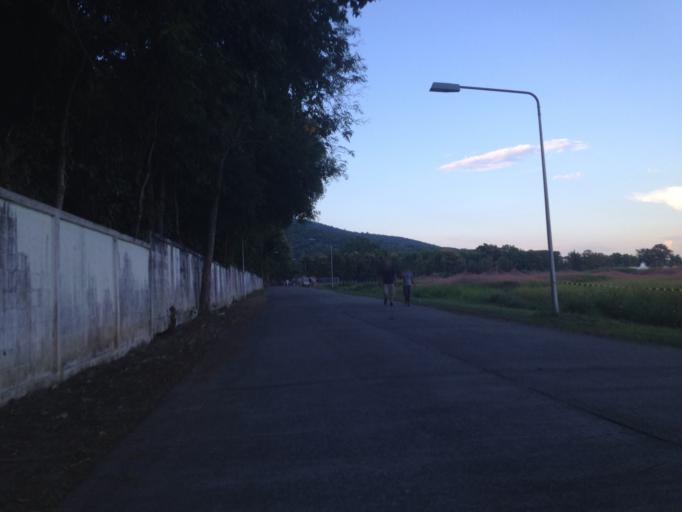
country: TH
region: Chiang Mai
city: Chiang Mai
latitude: 18.7606
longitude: 98.9269
